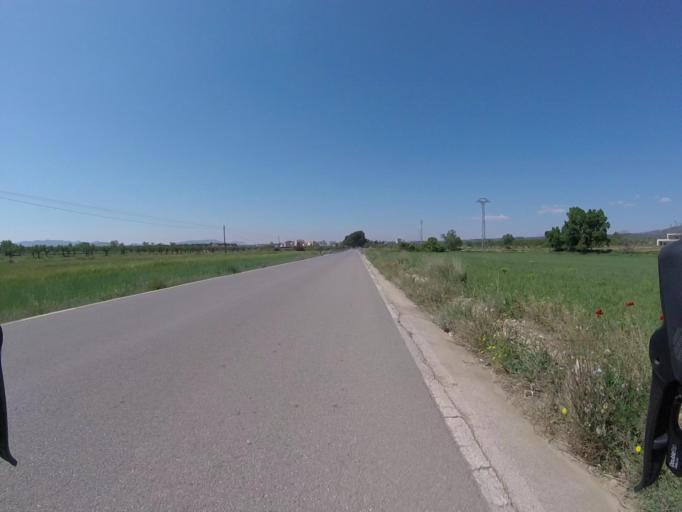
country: ES
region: Valencia
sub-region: Provincia de Castello
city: Benlloch
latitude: 40.2158
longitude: 0.0349
